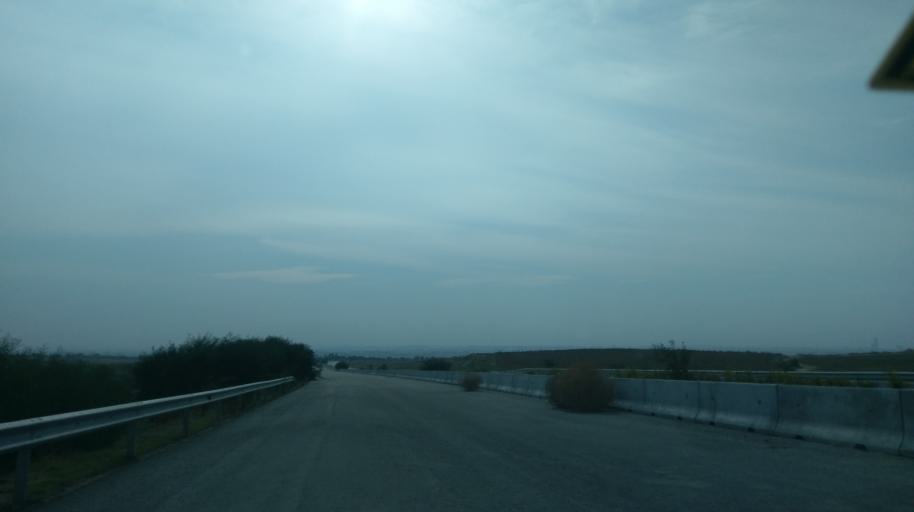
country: CY
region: Lefkosia
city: Nicosia
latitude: 35.2244
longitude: 33.4005
